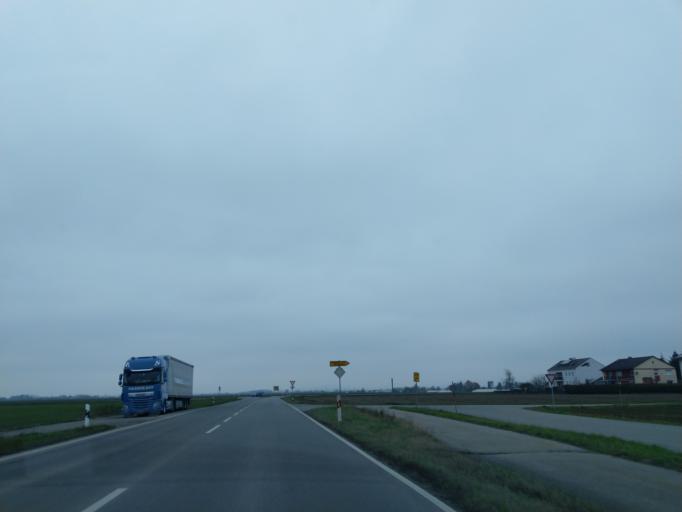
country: DE
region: Bavaria
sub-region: Lower Bavaria
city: Plattling
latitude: 48.8021
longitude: 12.8494
